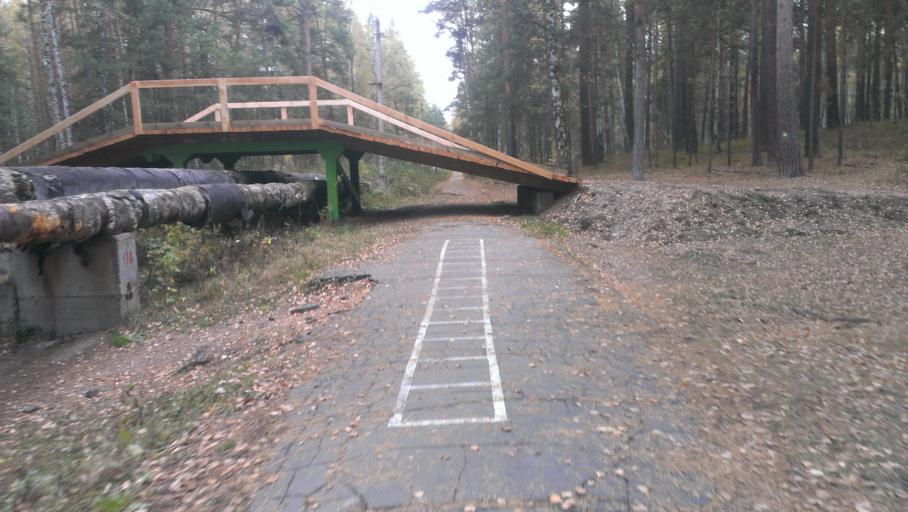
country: RU
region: Altai Krai
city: Yuzhnyy
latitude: 53.2652
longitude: 83.6848
